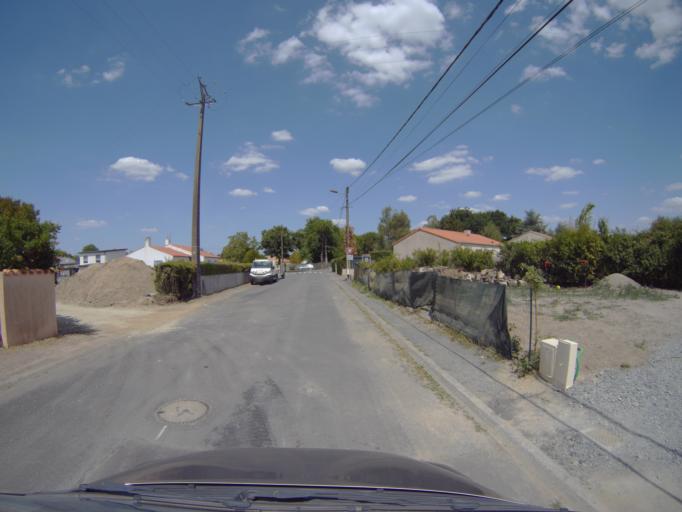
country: FR
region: Pays de la Loire
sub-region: Departement de la Loire-Atlantique
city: La Planche
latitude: 47.0161
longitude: -1.4316
